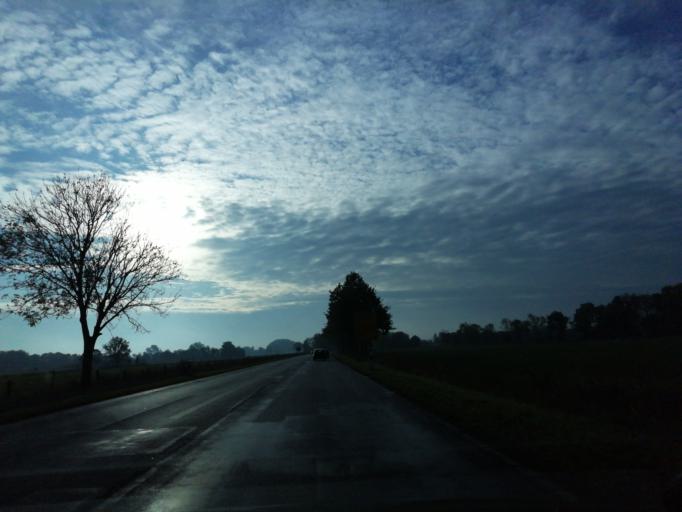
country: DE
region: Lower Saxony
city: Fedderwarden
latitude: 53.6026
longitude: 8.0476
